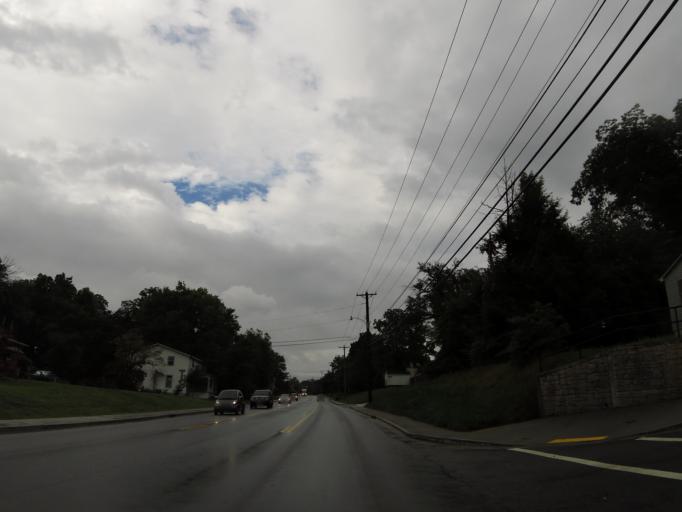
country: US
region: Tennessee
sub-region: Blount County
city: Maryville
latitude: 35.7588
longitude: -83.9536
